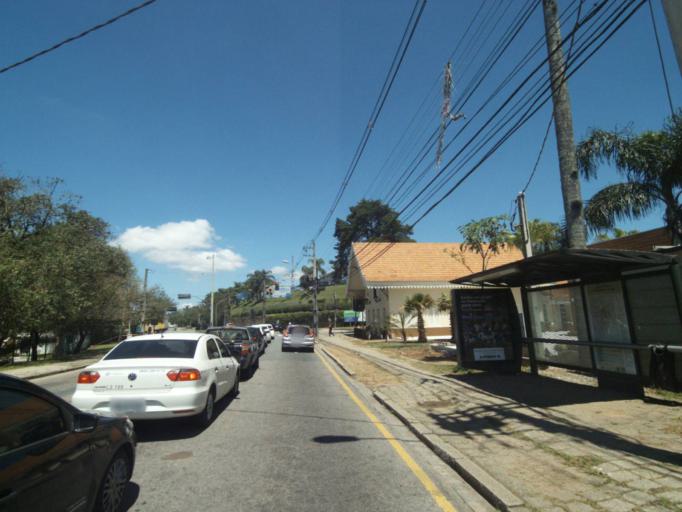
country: BR
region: Parana
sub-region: Curitiba
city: Curitiba
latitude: -25.3872
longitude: -49.2675
